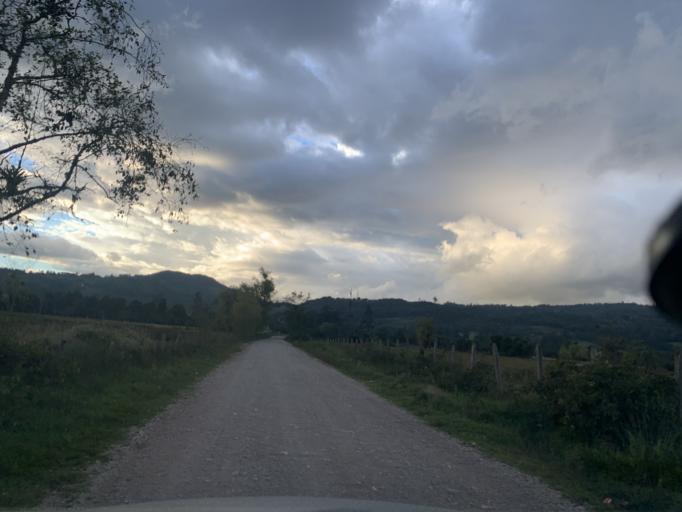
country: CO
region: Boyaca
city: La Capilla
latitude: 5.7338
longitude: -73.4967
